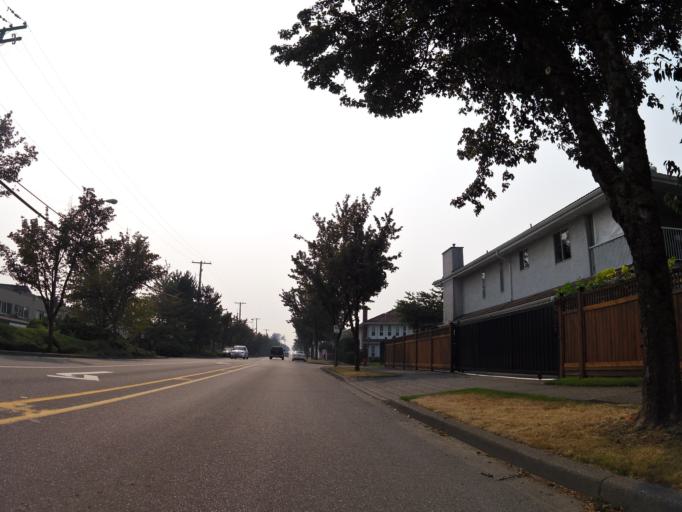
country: CA
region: British Columbia
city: Delta
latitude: 49.1516
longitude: -122.8791
